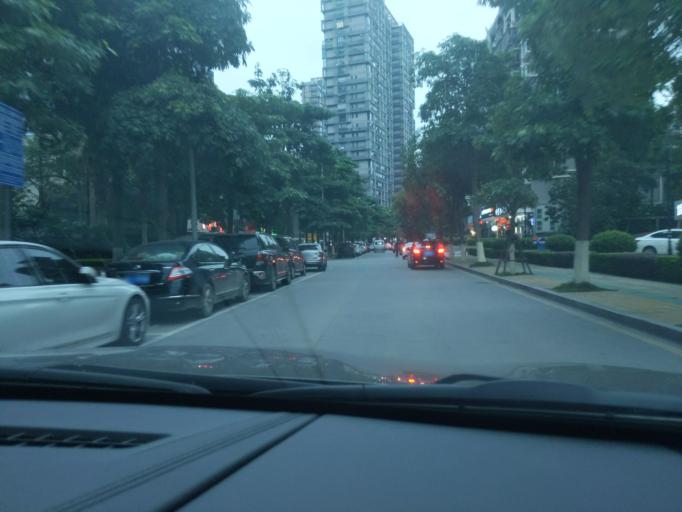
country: CN
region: Fujian
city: Xiamen
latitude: 24.4869
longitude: 118.1580
